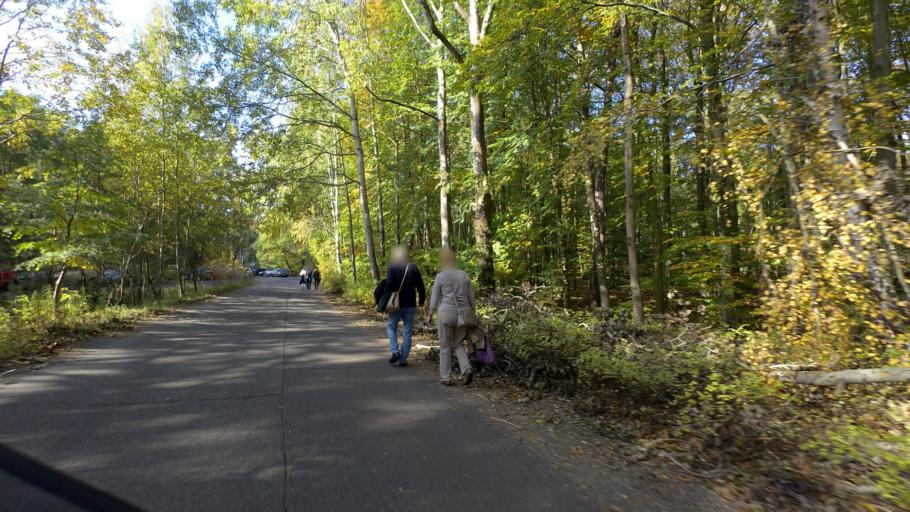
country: DE
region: Berlin
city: Friedrichshagen
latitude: 52.4185
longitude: 13.6162
